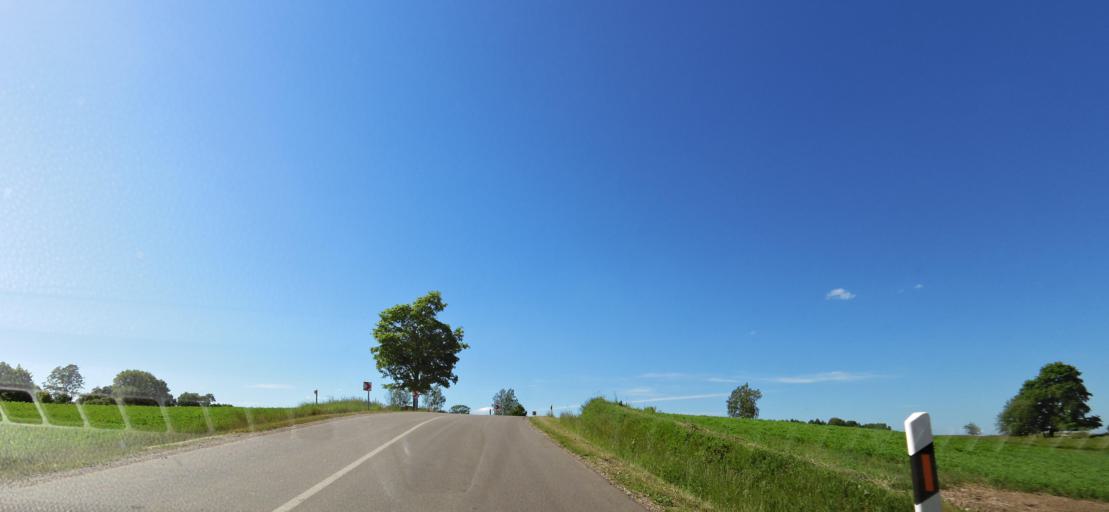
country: LT
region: Utenos apskritis
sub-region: Anyksciai
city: Anyksciai
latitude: 55.3691
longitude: 25.0968
